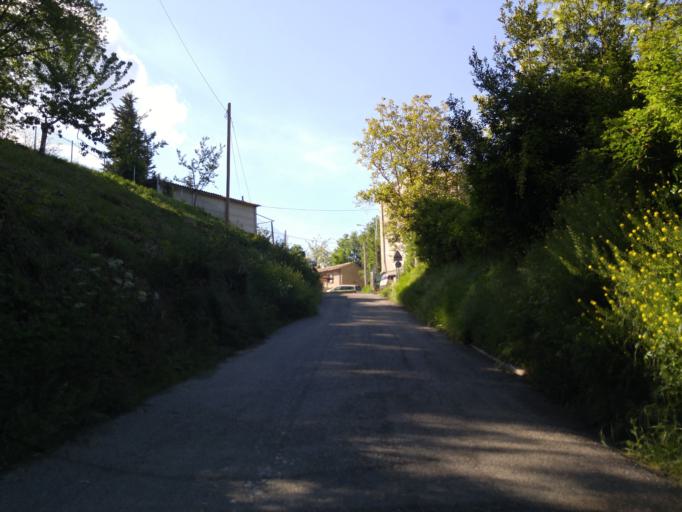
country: IT
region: The Marches
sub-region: Provincia di Pesaro e Urbino
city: Mombaroccio
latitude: 43.8085
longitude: 12.8503
